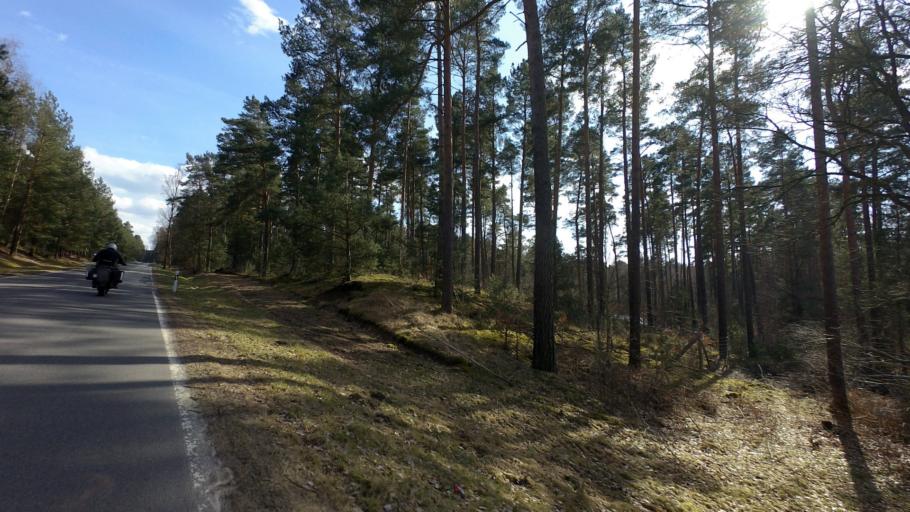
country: DE
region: Brandenburg
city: Marienwerder
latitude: 52.8068
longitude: 13.5859
